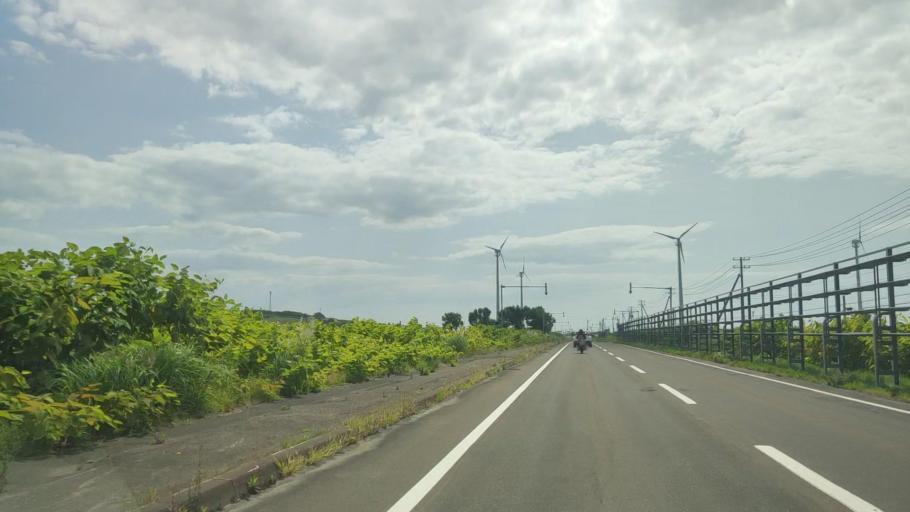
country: JP
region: Hokkaido
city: Rumoi
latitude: 44.3923
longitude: 141.7171
